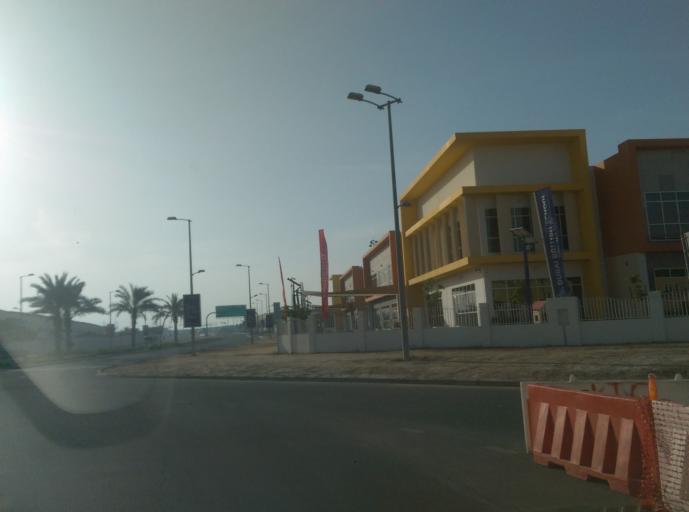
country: AE
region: Dubai
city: Dubai
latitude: 25.0449
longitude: 55.1575
